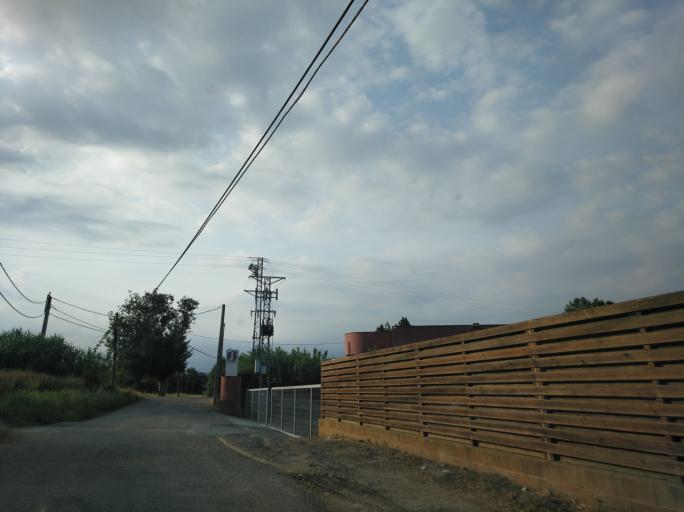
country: ES
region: Catalonia
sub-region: Provincia de Girona
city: la Cellera de Ter
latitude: 41.9625
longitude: 2.6222
